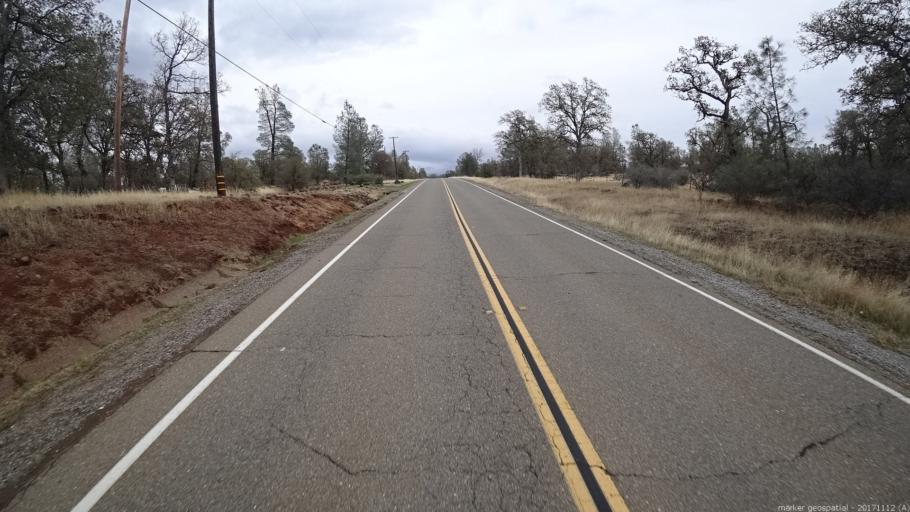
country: US
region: California
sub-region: Shasta County
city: Palo Cedro
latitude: 40.4882
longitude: -122.1299
